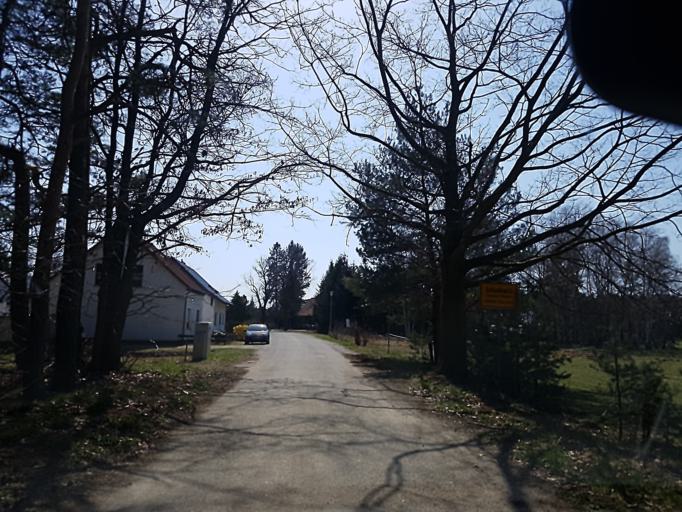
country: DE
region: Brandenburg
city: Schonborn
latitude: 51.5654
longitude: 13.4822
